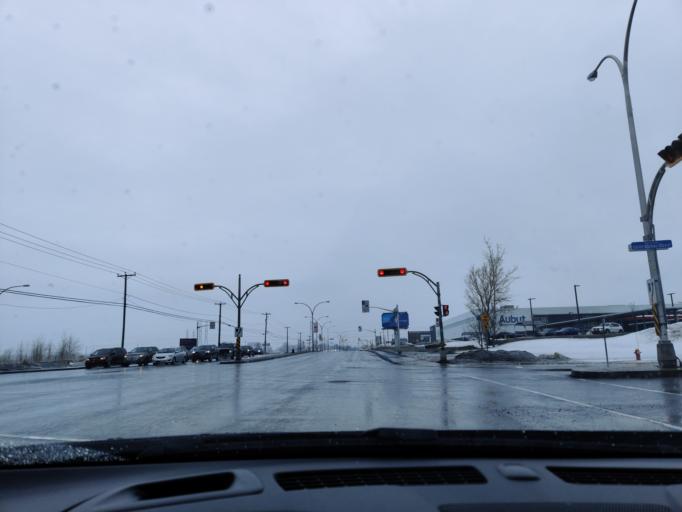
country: CA
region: Quebec
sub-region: Laurentides
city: Rosemere
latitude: 45.5690
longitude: -73.7816
